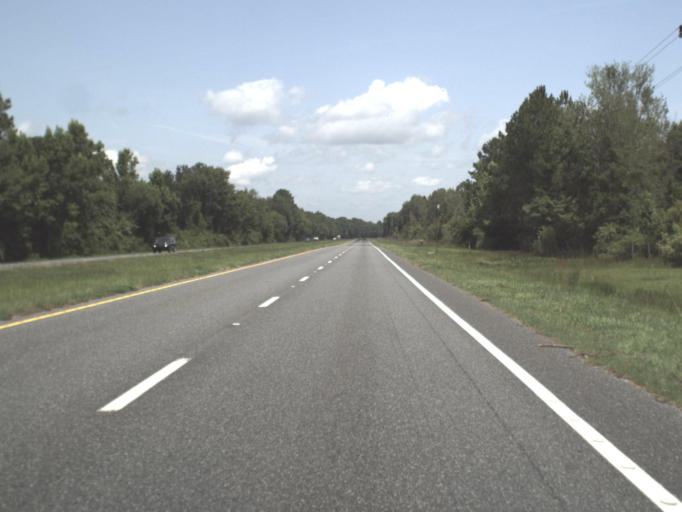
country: US
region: Florida
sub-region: Taylor County
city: Perry
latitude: 29.9226
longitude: -83.4382
